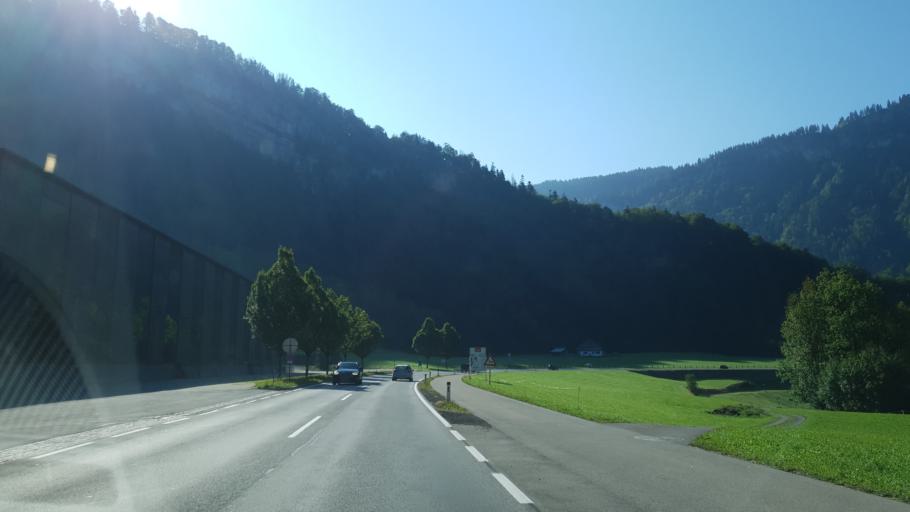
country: AT
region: Vorarlberg
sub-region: Politischer Bezirk Bregenz
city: Andelsbuch
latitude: 47.3964
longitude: 9.8545
